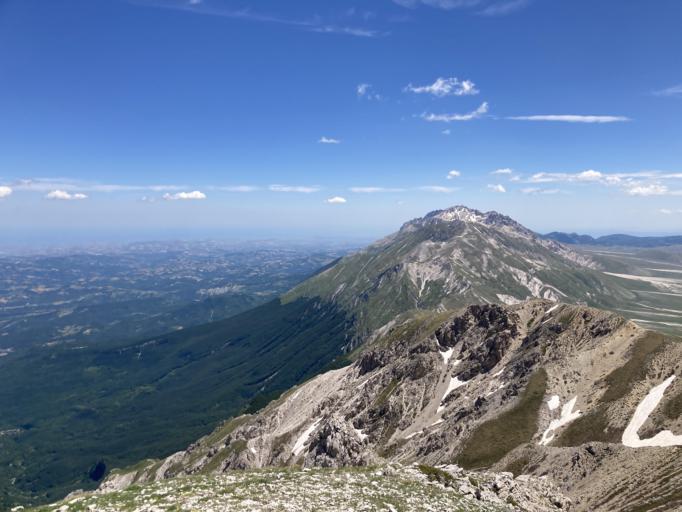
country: IT
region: Abruzzo
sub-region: Provincia di Teramo
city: Pietracamela
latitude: 42.4563
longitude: 13.5686
